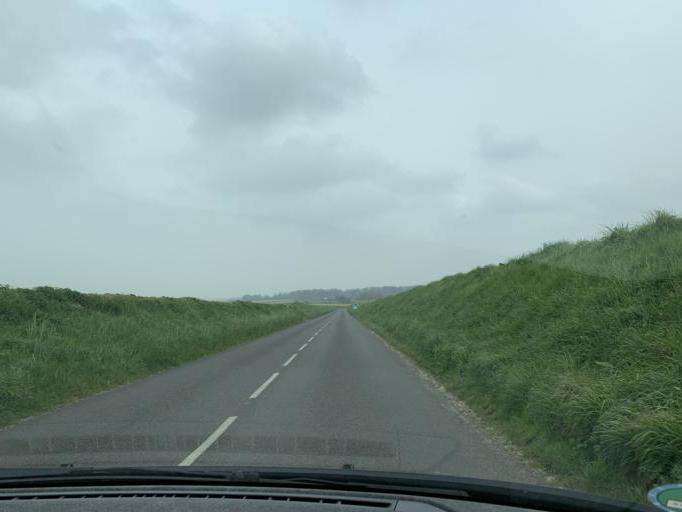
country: FR
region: Haute-Normandie
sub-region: Departement de la Seine-Maritime
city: Saint-Valery-en-Caux
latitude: 49.8551
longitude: 0.7698
